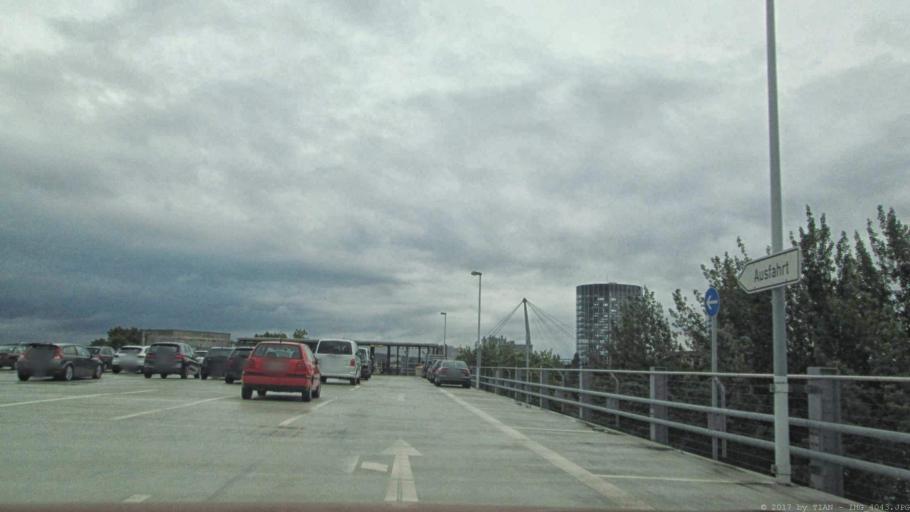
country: DE
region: Lower Saxony
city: Wolfsburg
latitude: 52.4366
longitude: 10.7964
